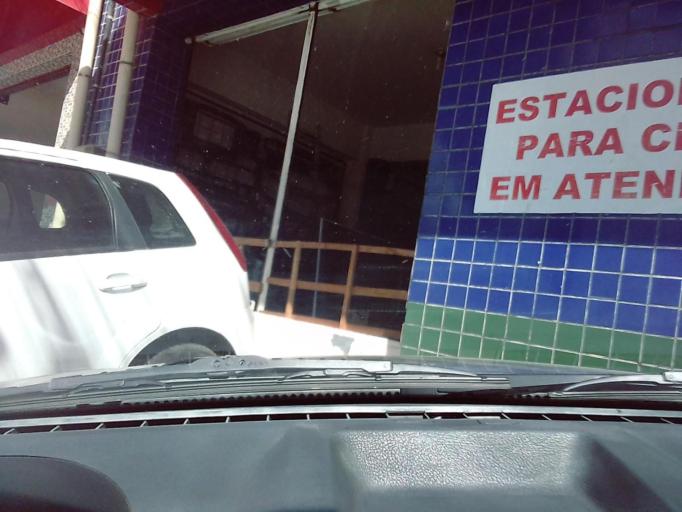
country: BR
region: Pernambuco
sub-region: Vitoria De Santo Antao
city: Vitoria de Santo Antao
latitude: -8.1174
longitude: -35.2976
